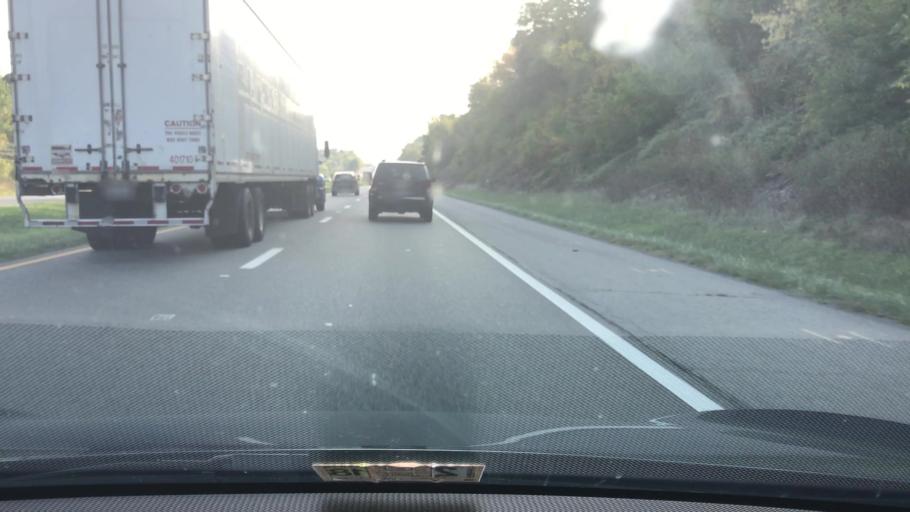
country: US
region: Virginia
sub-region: Botetourt County
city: Laymantown
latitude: 37.3341
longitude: -79.8606
